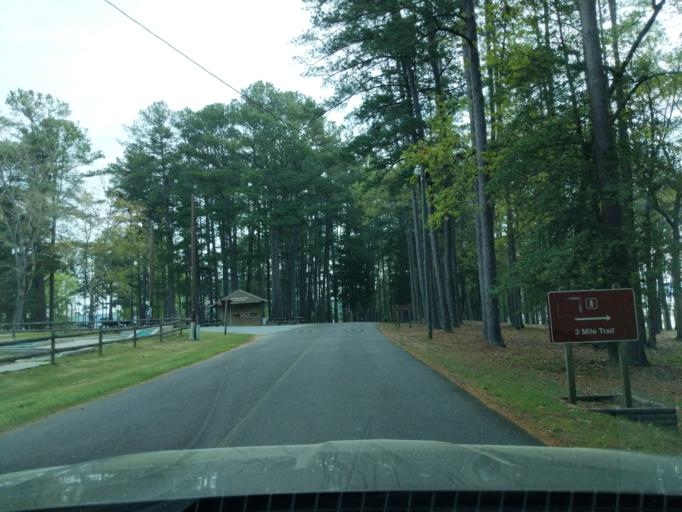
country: US
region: Georgia
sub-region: Lincoln County
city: Lincolnton
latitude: 33.8549
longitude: -82.4022
